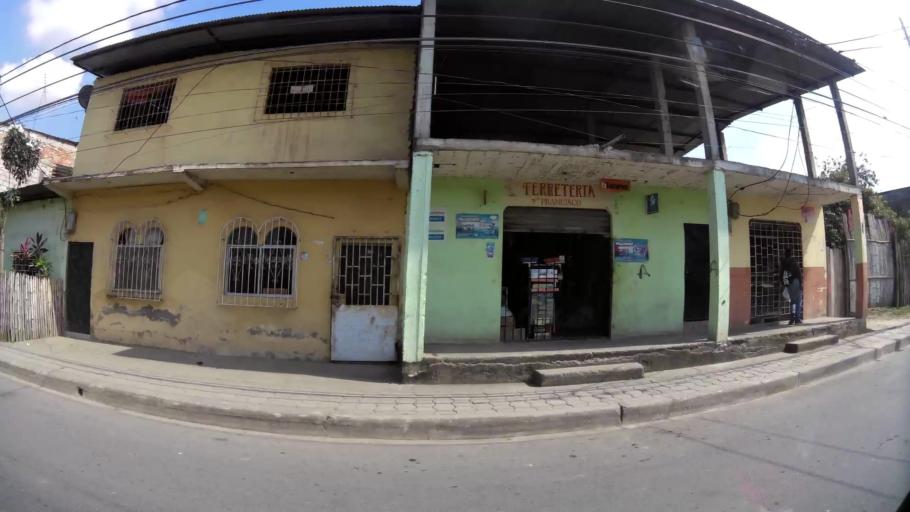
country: EC
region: Guayas
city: Eloy Alfaro
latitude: -2.1720
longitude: -79.8282
